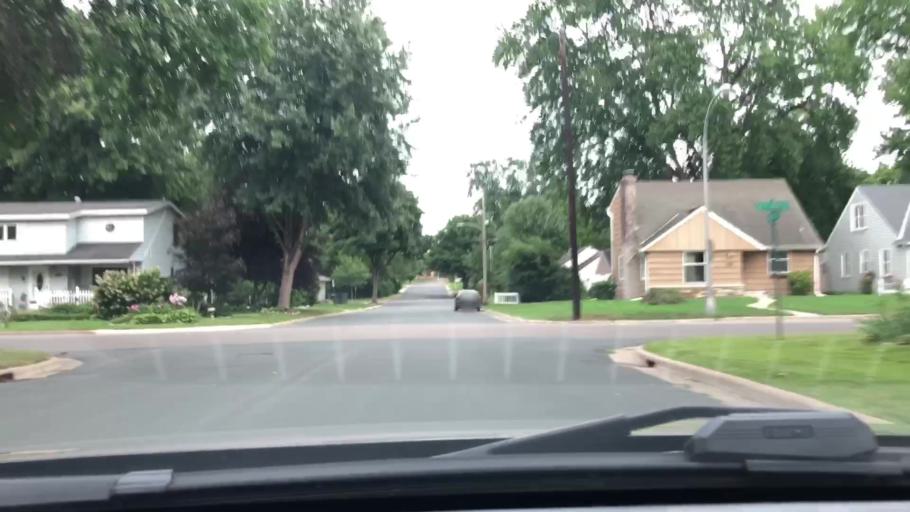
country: US
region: Minnesota
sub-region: Hennepin County
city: Richfield
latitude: 44.8727
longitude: -93.2746
